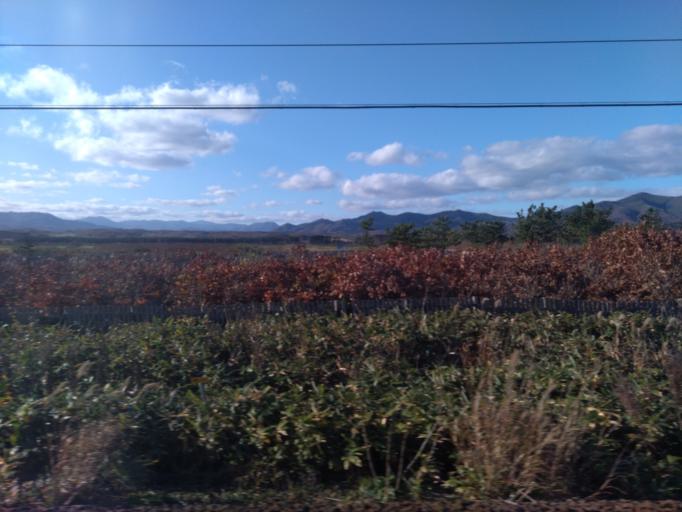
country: JP
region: Hokkaido
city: Niseko Town
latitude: 42.5431
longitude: 140.4091
